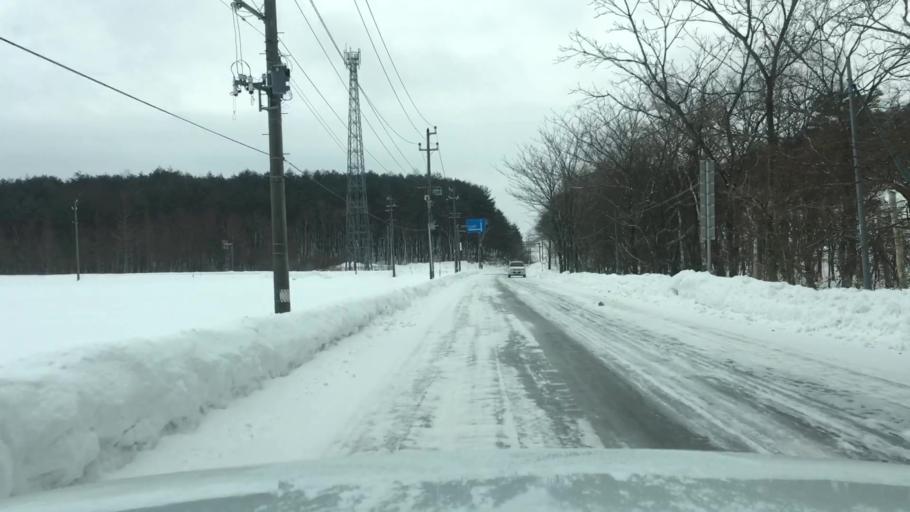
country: JP
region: Iwate
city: Shizukuishi
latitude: 39.9713
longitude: 141.0006
